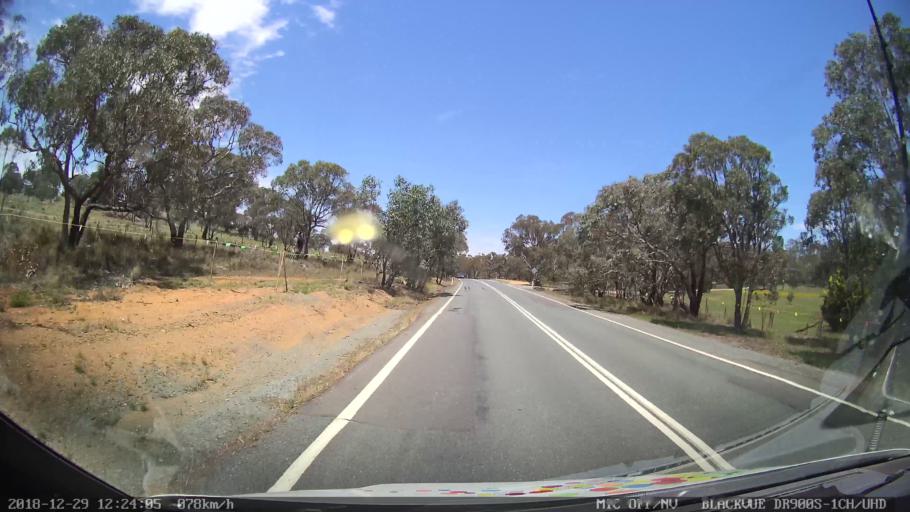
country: AU
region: New South Wales
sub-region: Queanbeyan
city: Queanbeyan
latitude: -35.4435
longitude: 149.2134
